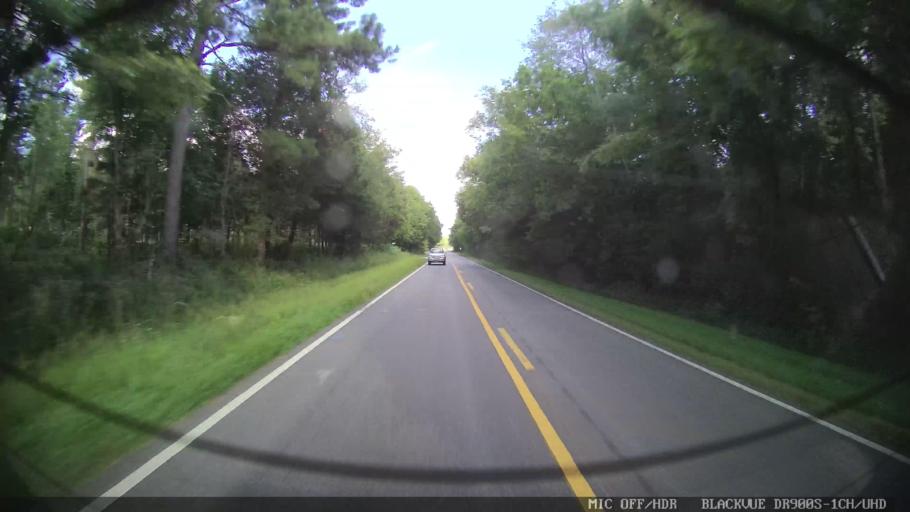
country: US
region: Georgia
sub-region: Bartow County
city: Euharlee
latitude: 34.1827
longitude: -85.0407
